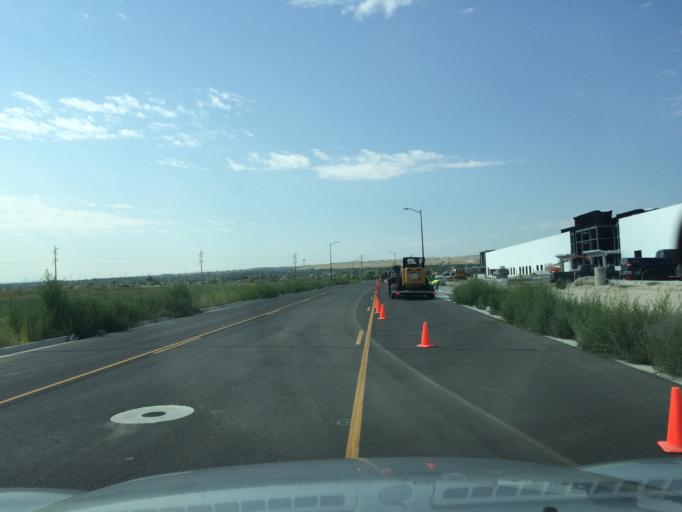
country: US
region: Utah
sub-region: Salt Lake County
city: Magna
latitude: 40.7183
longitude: -112.0526
